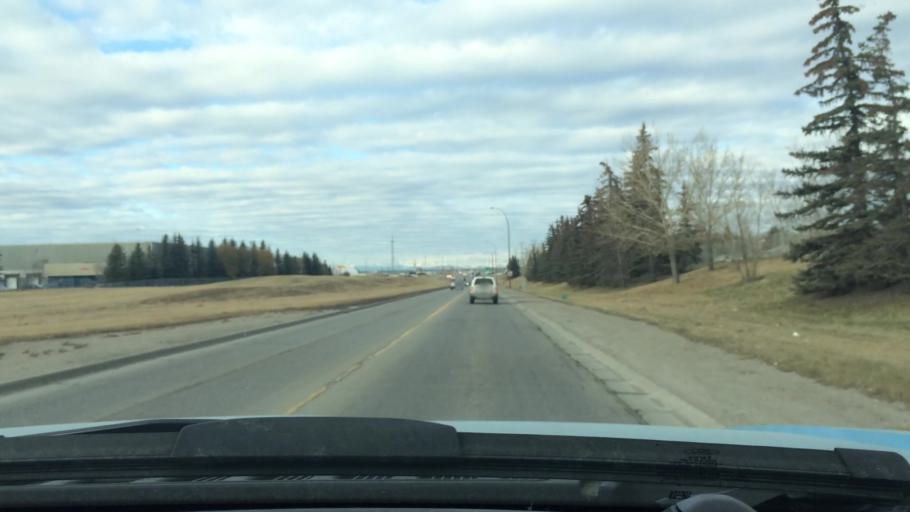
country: CA
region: Alberta
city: Calgary
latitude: 51.0155
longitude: -113.9912
